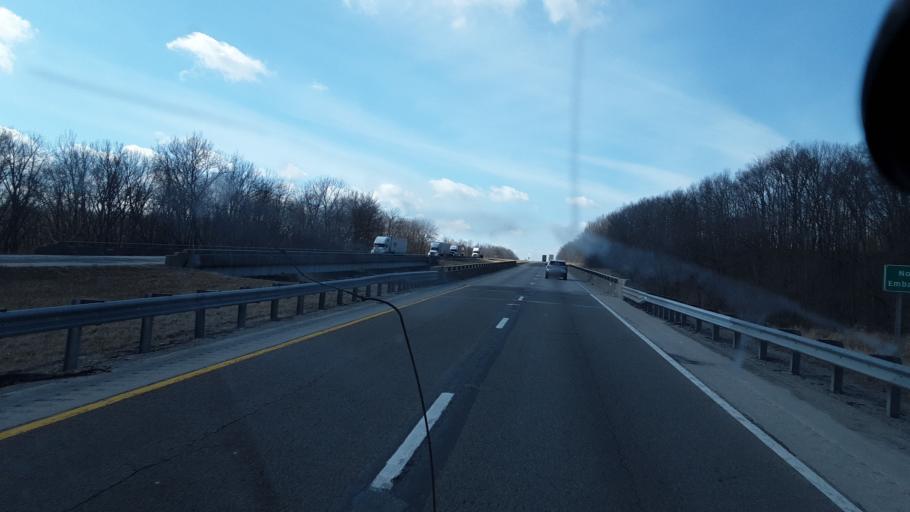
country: US
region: Illinois
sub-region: Clark County
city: Martinsville
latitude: 39.3523
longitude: -87.9022
